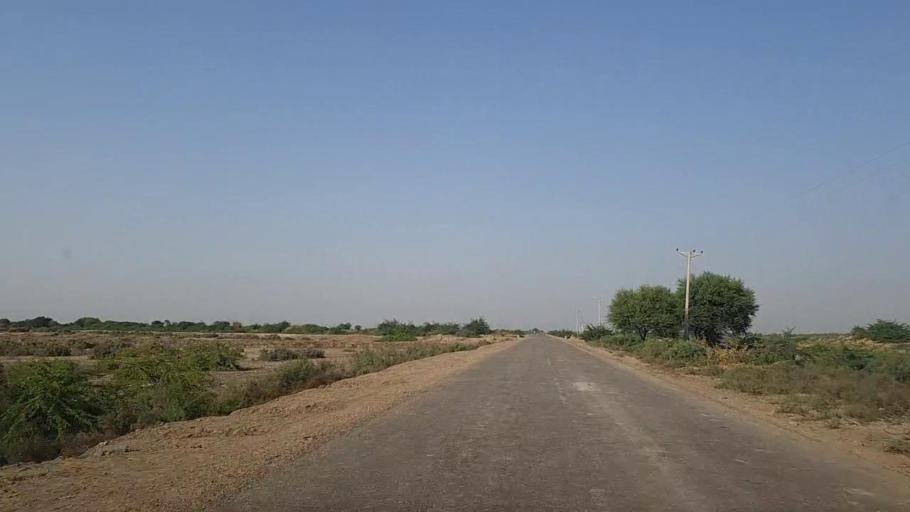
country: PK
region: Sindh
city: Mirpur Batoro
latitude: 24.6127
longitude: 68.4040
